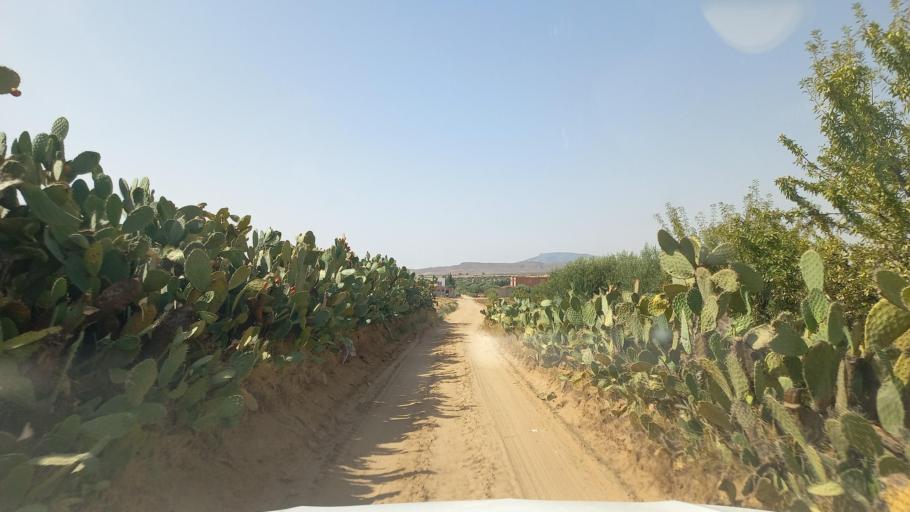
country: TN
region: Al Qasrayn
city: Kasserine
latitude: 35.2358
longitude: 9.0446
